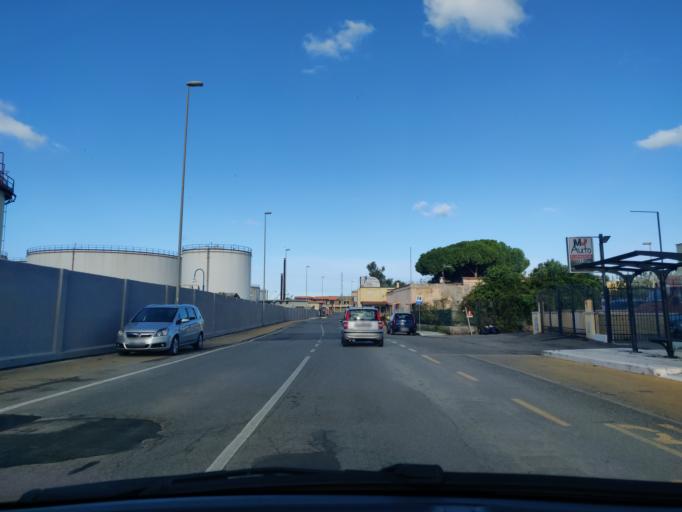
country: IT
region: Latium
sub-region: Citta metropolitana di Roma Capitale
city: Civitavecchia
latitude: 42.1074
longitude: 11.7809
